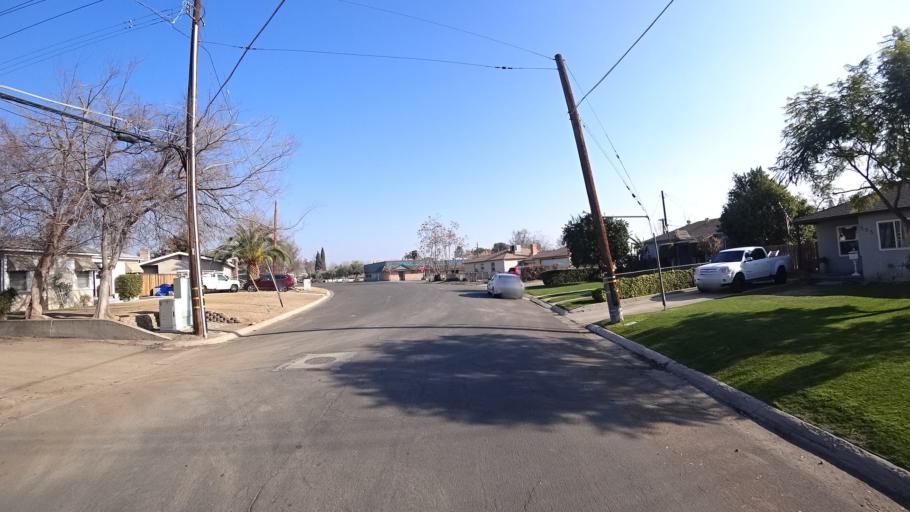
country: US
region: California
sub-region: Kern County
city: Bakersfield
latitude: 35.3946
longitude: -118.9949
